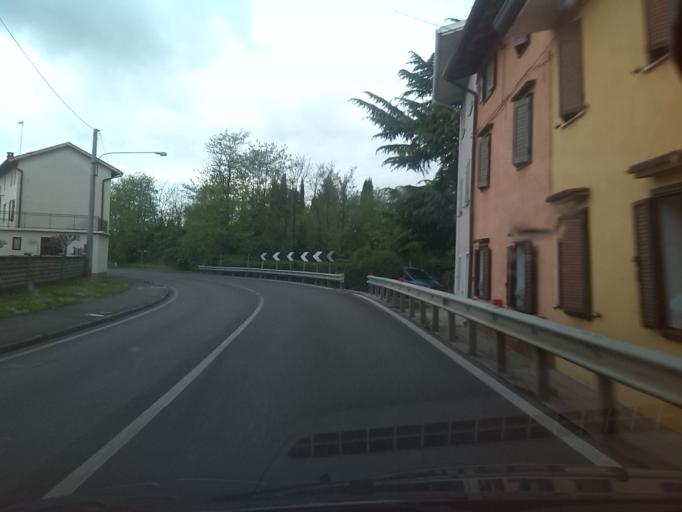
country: IT
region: Friuli Venezia Giulia
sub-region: Provincia di Gorizia
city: Capriva del Friuli
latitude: 45.9384
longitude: 13.5174
